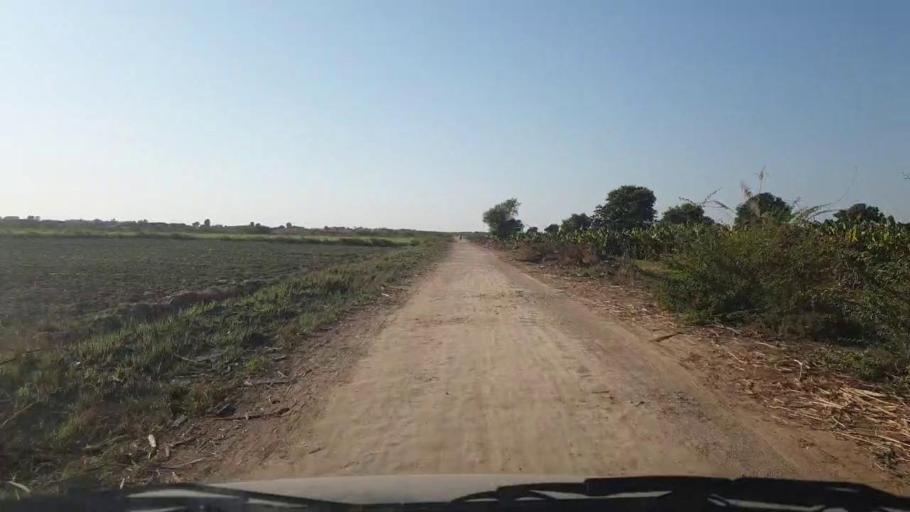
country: PK
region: Sindh
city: Samaro
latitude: 25.3589
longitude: 69.2990
